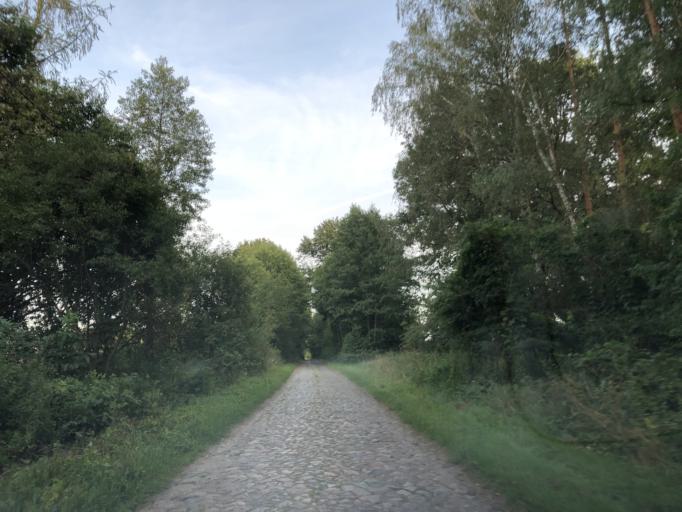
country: PL
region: Lubusz
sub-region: Powiat swiebodzinski
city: Zbaszynek
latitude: 52.2347
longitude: 15.7933
